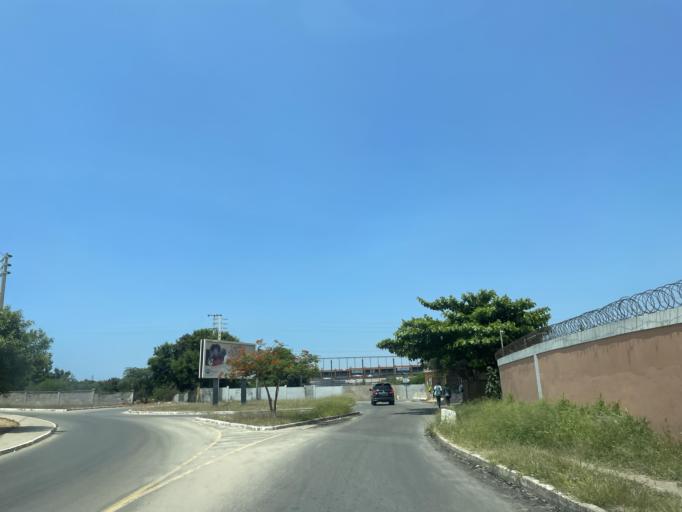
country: AO
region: Luanda
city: Luanda
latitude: -8.9185
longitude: 13.2052
